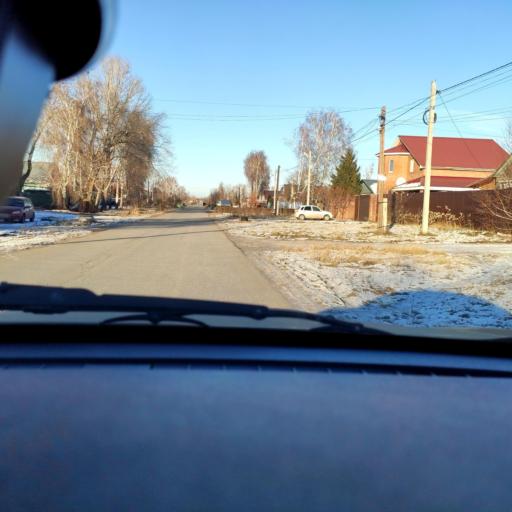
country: RU
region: Samara
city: Tol'yatti
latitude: 53.5579
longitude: 49.3980
